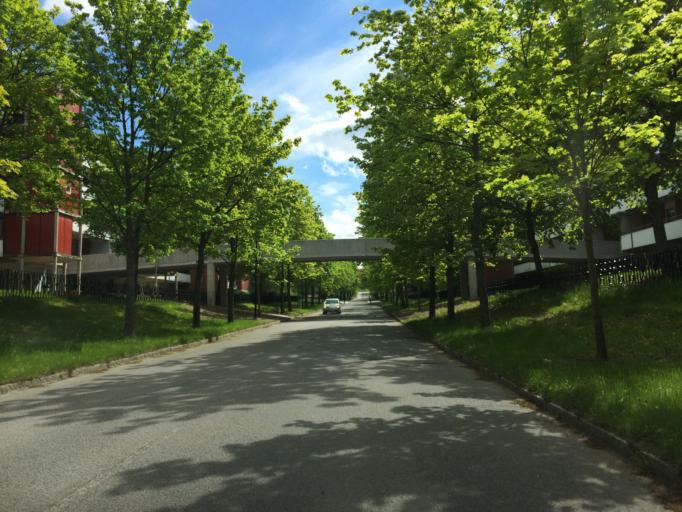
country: SE
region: Stockholm
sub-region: Botkyrka Kommun
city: Fittja
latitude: 59.2674
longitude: 17.8877
